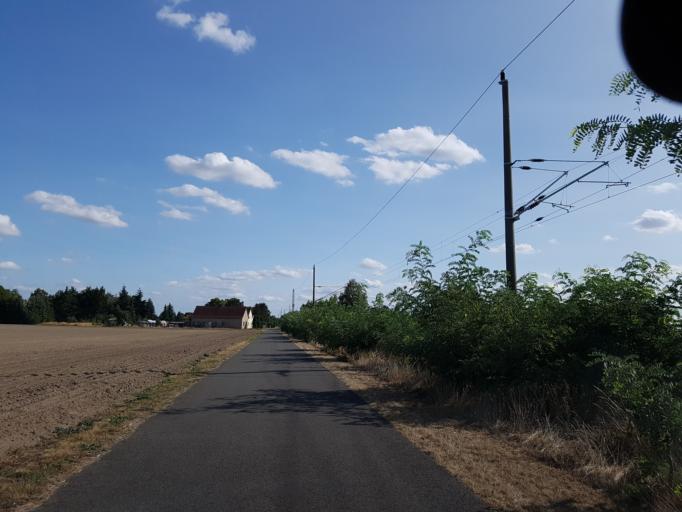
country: DE
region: Brandenburg
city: Juterbog
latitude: 51.8967
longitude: 13.0660
